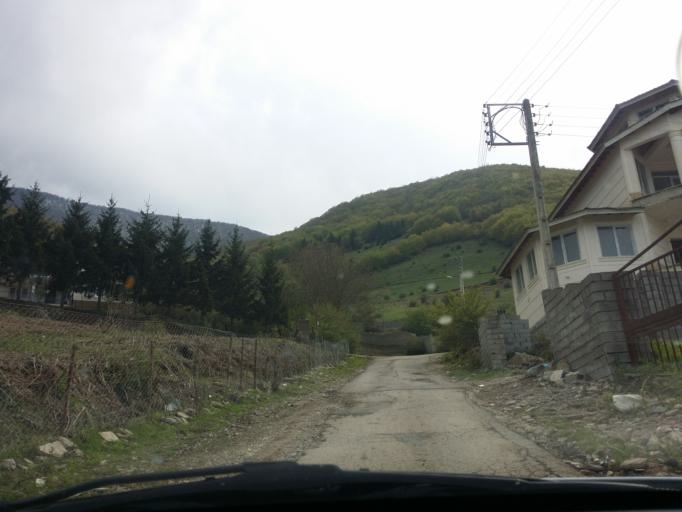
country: IR
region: Mazandaran
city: `Abbasabad
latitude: 36.4854
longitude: 51.1517
